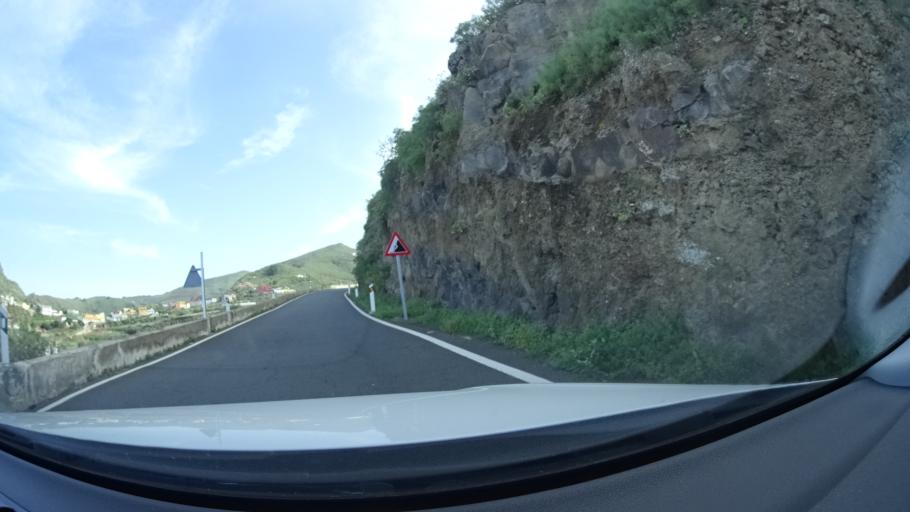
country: ES
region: Canary Islands
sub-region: Provincia de Las Palmas
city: Guia
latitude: 28.1162
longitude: -15.6421
